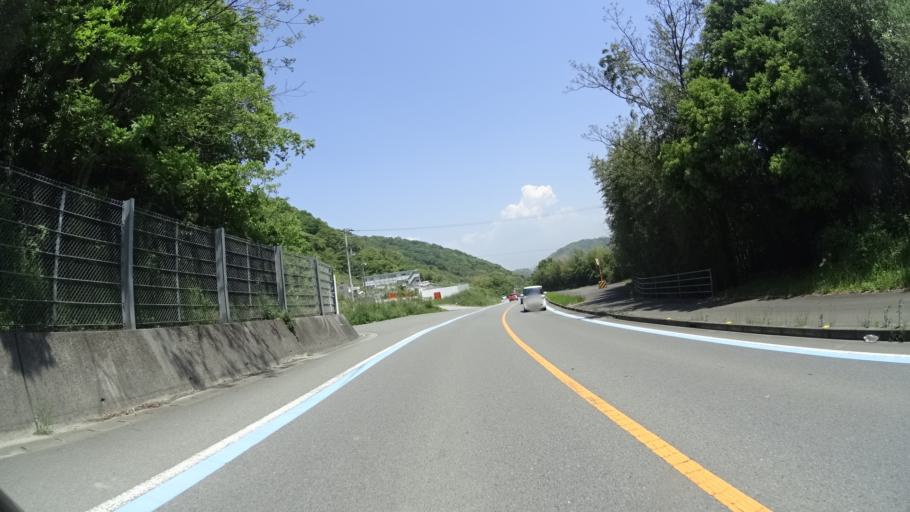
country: JP
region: Ehime
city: Iyo
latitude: 33.7245
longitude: 132.6826
